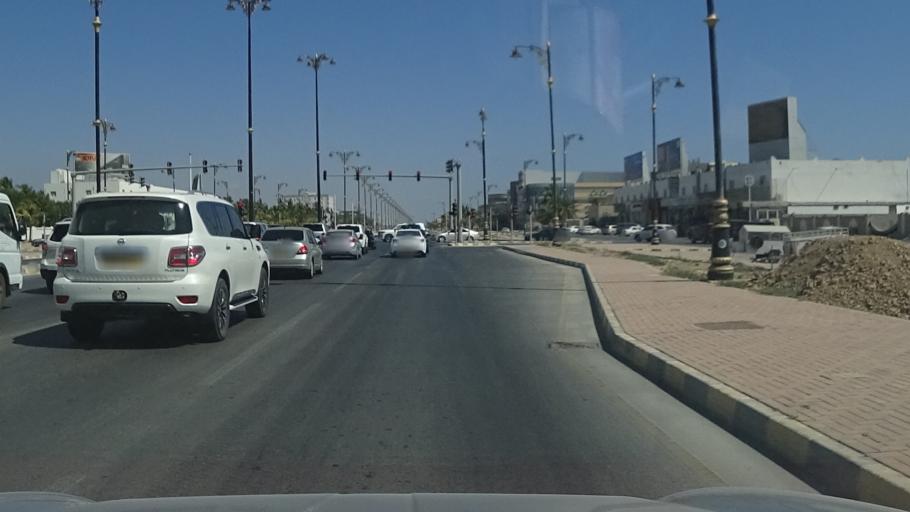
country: OM
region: Zufar
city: Salalah
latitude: 17.0361
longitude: 54.1595
